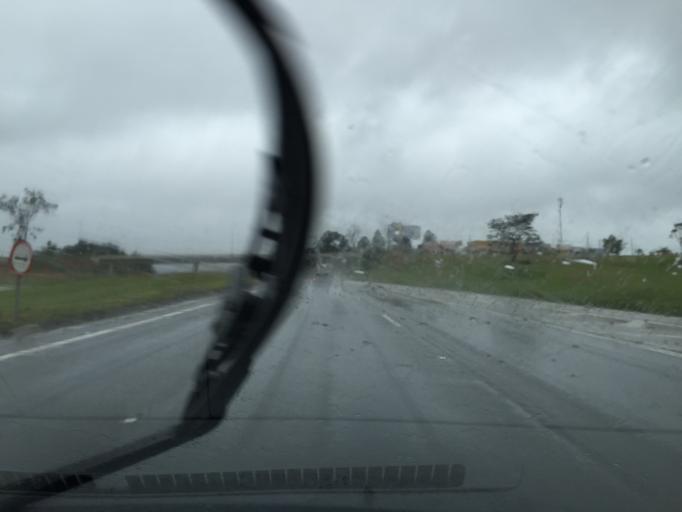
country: BR
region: Sao Paulo
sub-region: Mairinque
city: Mairinque
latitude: -23.4222
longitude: -47.2470
